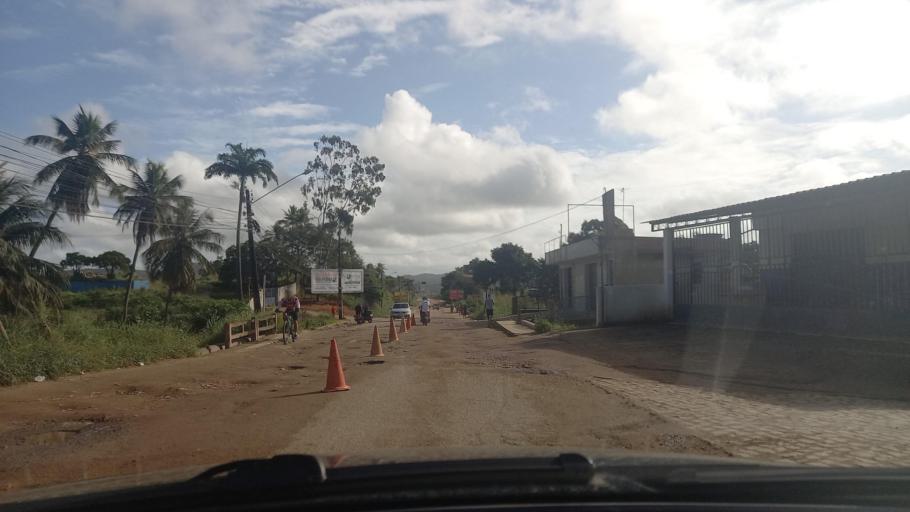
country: BR
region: Pernambuco
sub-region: Vitoria De Santo Antao
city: Vitoria de Santo Antao
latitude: -8.1214
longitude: -35.2821
